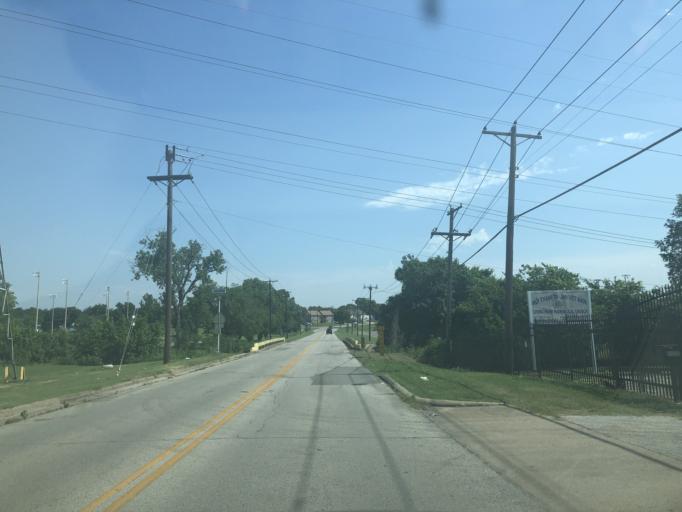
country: US
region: Texas
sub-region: Dallas County
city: Grand Prairie
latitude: 32.7254
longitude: -97.0072
